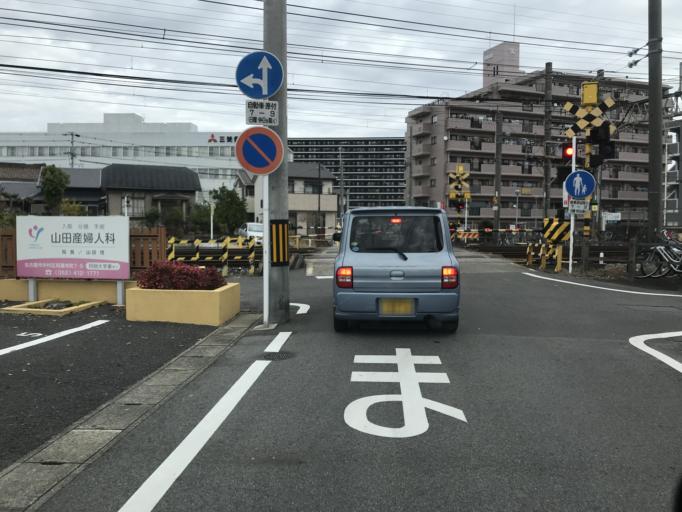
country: JP
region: Aichi
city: Nagoya-shi
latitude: 35.1946
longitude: 136.8584
